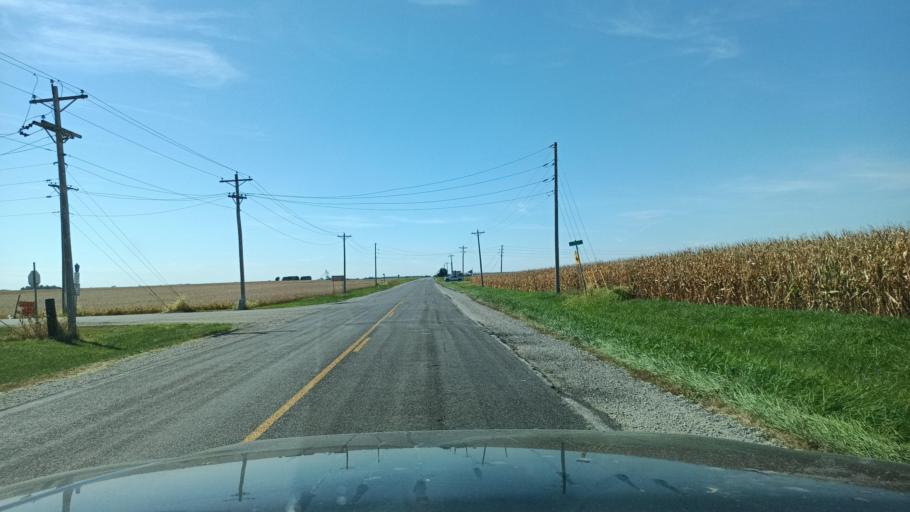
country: US
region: Illinois
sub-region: De Witt County
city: Farmer City
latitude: 40.2240
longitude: -88.7440
